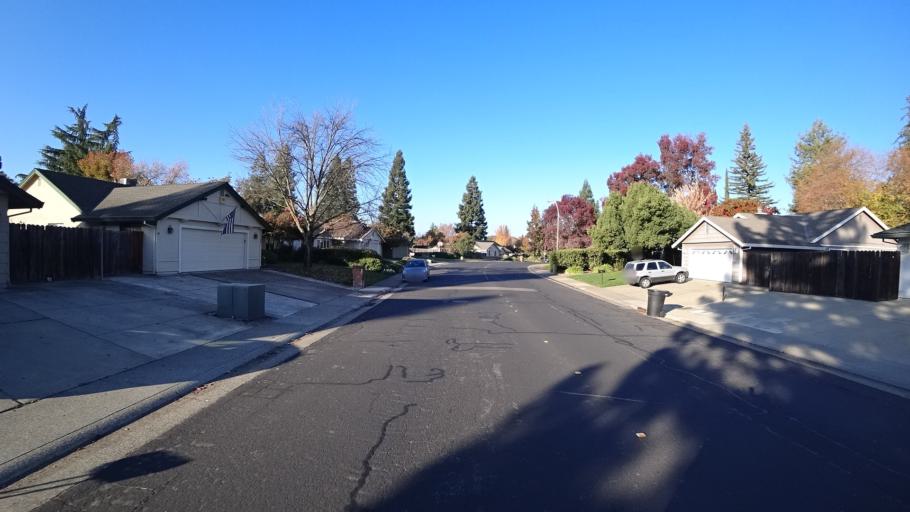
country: US
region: California
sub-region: Sacramento County
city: Citrus Heights
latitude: 38.7199
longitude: -121.2590
